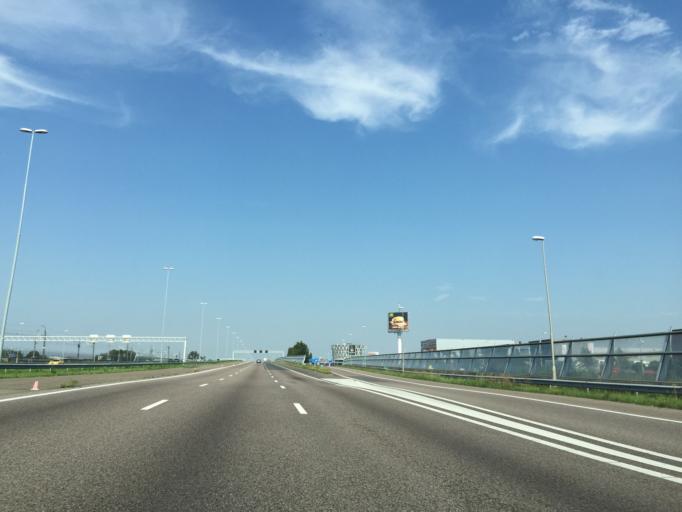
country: NL
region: South Holland
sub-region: Gemeente Kaag en Braassem
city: Oude Wetering
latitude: 52.1954
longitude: 4.6106
